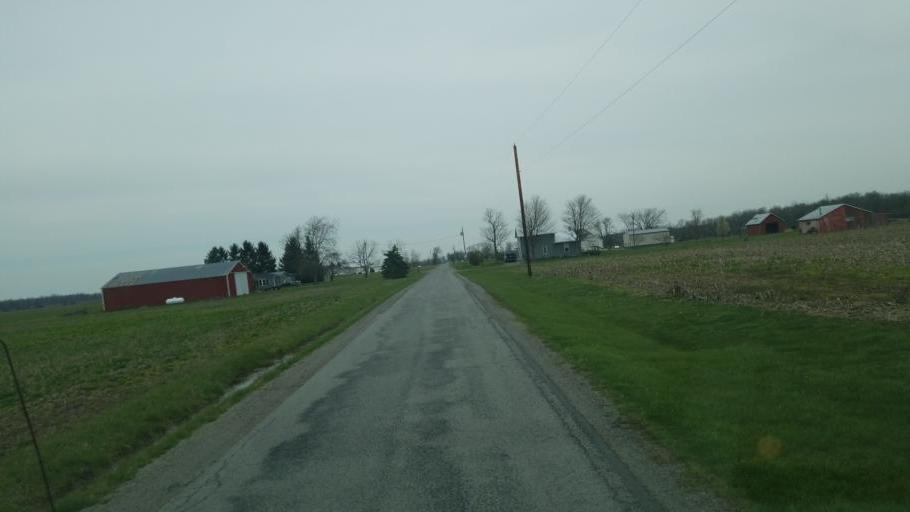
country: US
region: Ohio
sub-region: Hardin County
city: Forest
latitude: 40.8950
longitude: -83.5149
